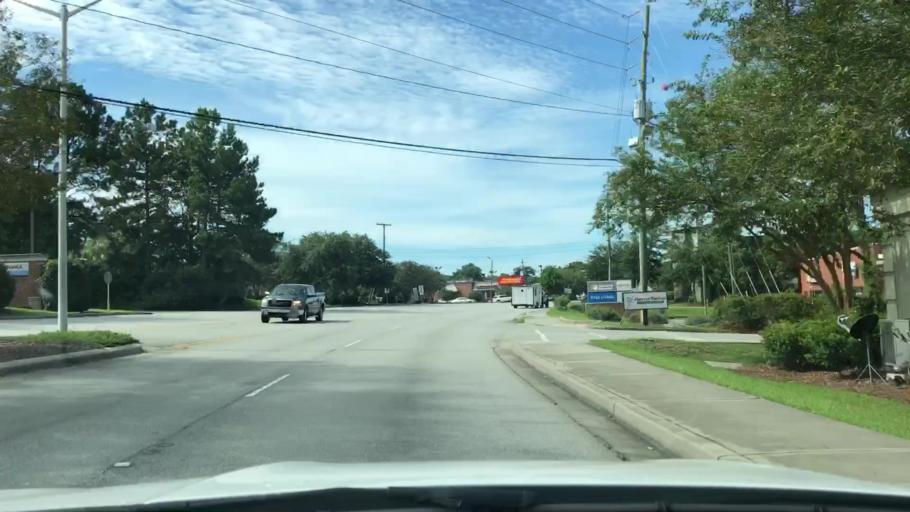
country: US
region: South Carolina
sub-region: Dorchester County
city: Centerville
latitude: 32.9994
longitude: -80.1841
